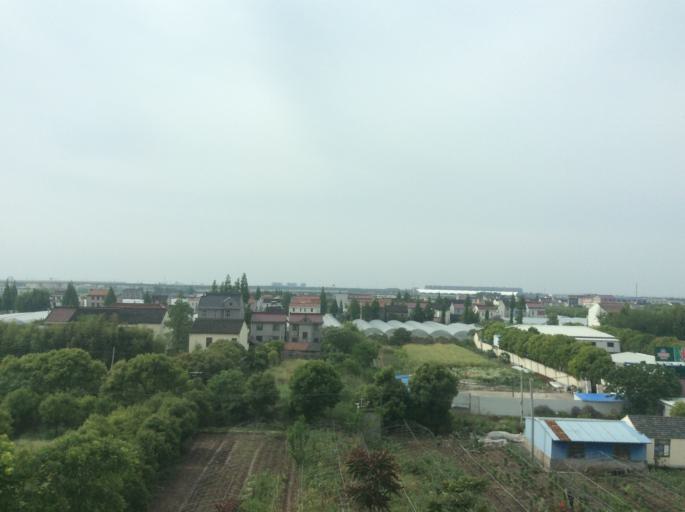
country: CN
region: Shanghai Shi
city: Kangqiao
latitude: 31.2104
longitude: 121.7516
